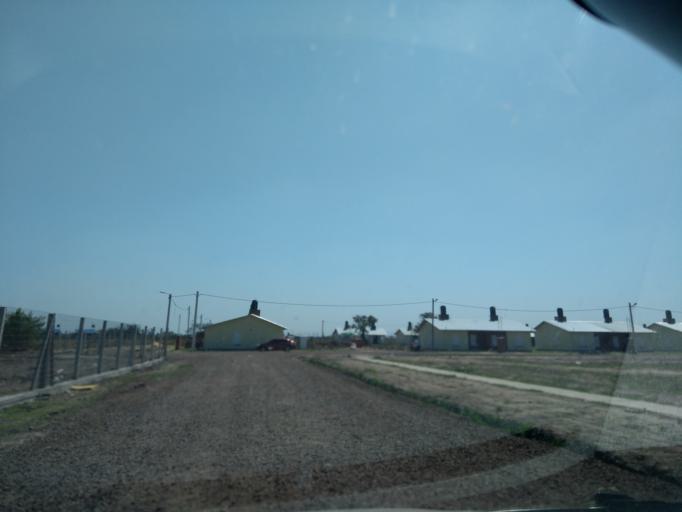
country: AR
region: Chaco
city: Fontana
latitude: -27.4080
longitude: -58.9744
